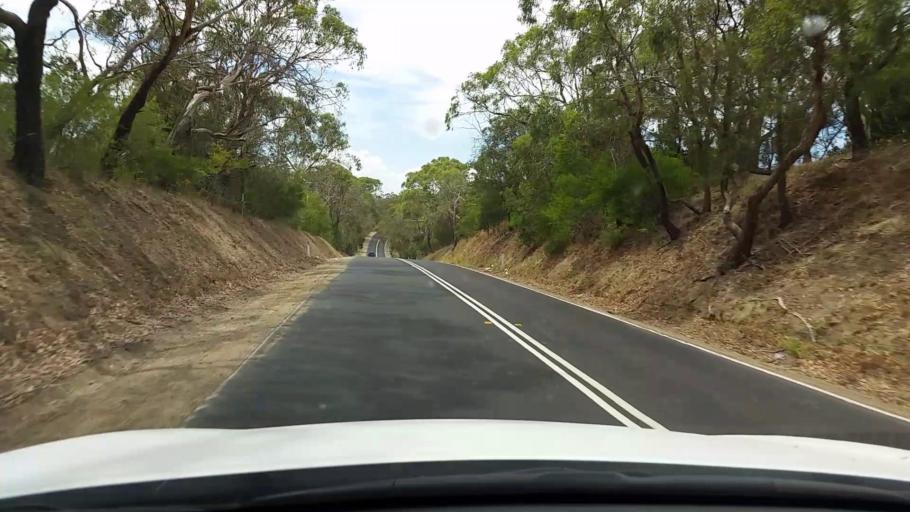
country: AU
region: Victoria
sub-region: Mornington Peninsula
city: Mount Martha
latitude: -38.2990
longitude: 145.0438
